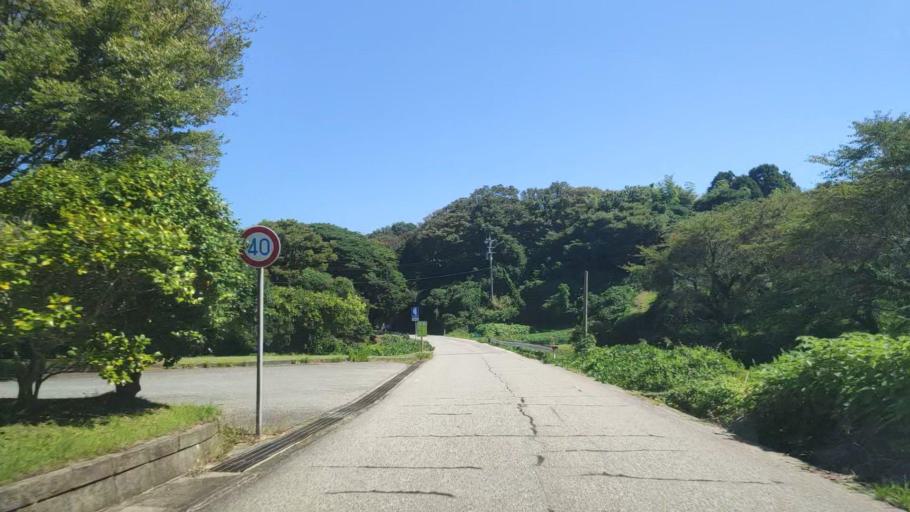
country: JP
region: Ishikawa
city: Nanao
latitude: 37.5255
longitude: 137.2624
